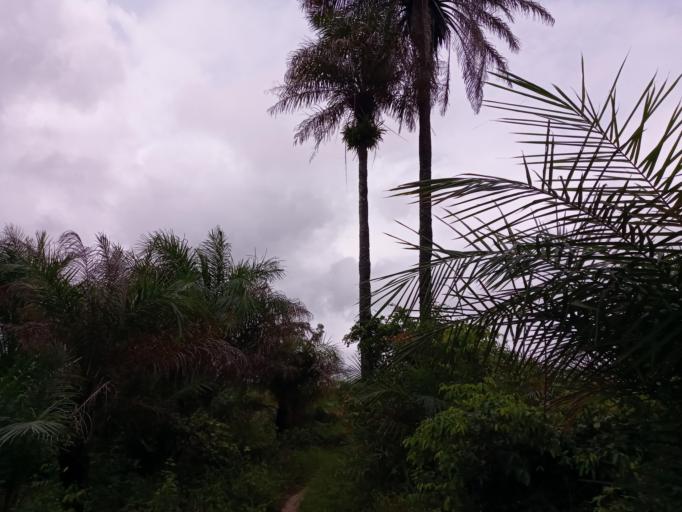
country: SL
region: Southern Province
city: Bonthe
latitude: 7.5213
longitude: -12.5735
